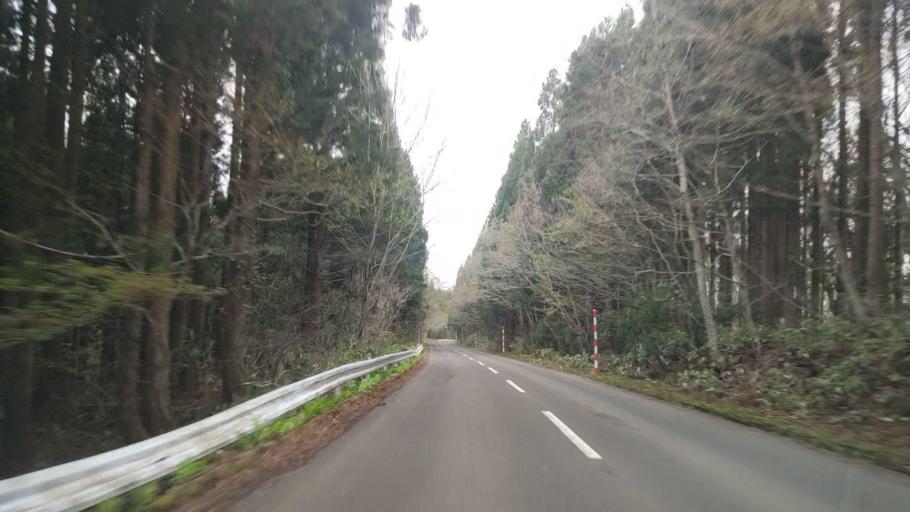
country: JP
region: Akita
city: Hanawa
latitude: 40.3927
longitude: 140.7952
